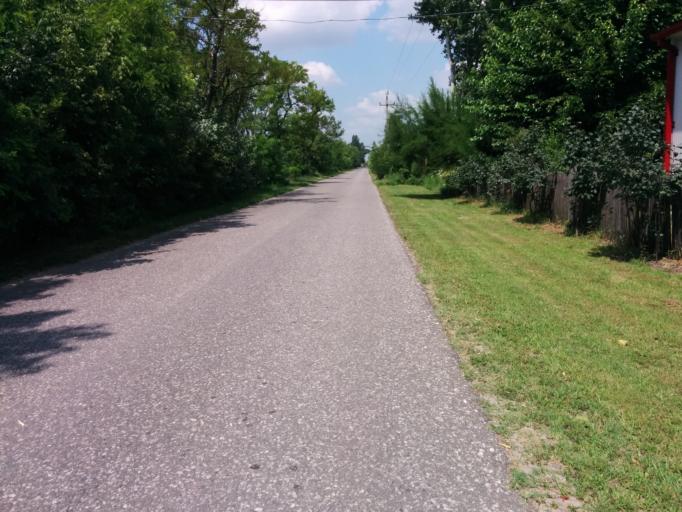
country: HU
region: Csongrad
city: Zakanyszek
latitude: 46.2678
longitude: 19.8989
